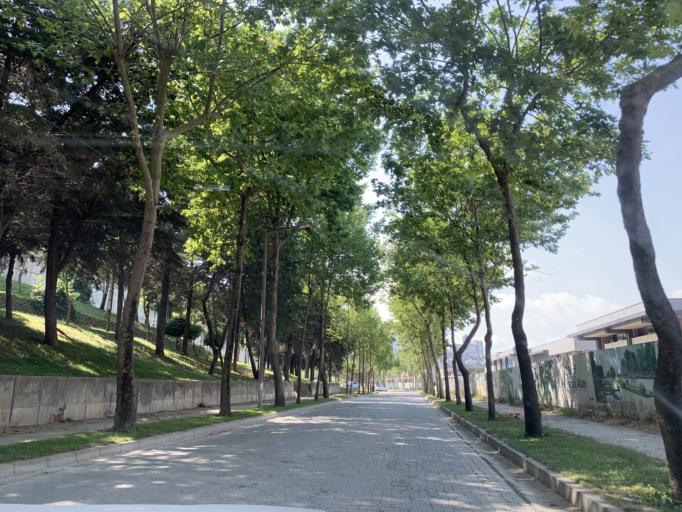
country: TR
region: Istanbul
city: Esenyurt
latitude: 41.0633
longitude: 28.6970
